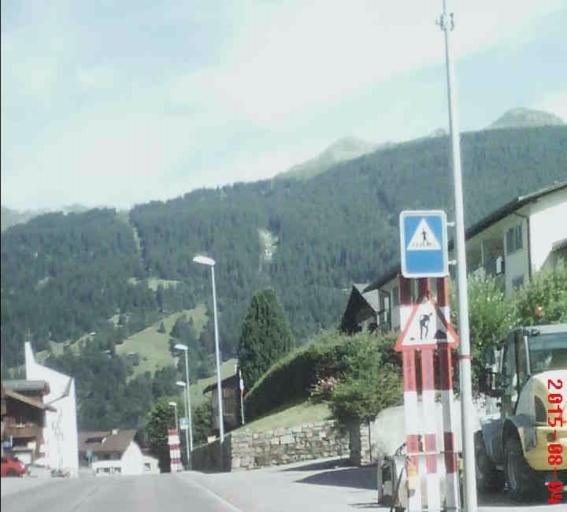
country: CH
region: Grisons
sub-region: Praettigau/Davos District
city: Klosters Serneus
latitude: 46.8708
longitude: 9.8818
